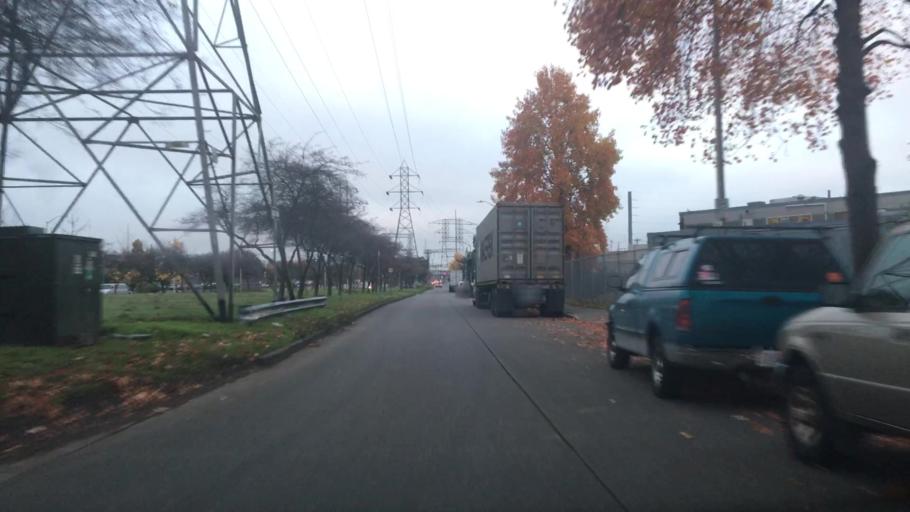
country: US
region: Washington
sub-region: King County
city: Seattle
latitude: 47.5656
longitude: -122.3240
